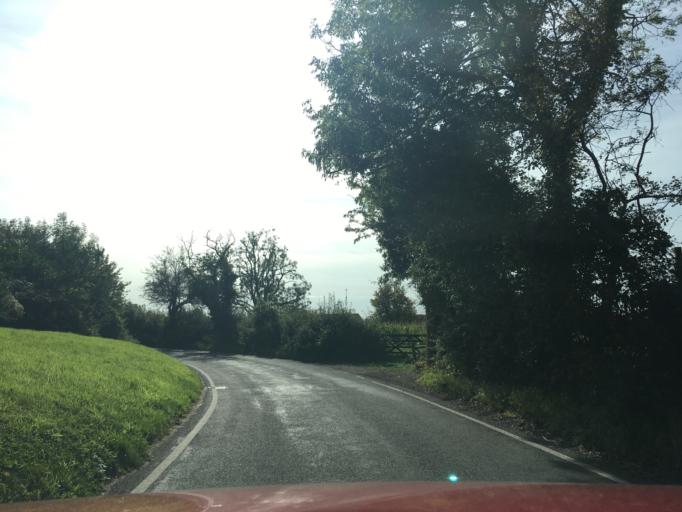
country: GB
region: England
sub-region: South Gloucestershire
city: Chipping Sodbury
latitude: 51.5557
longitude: -2.4036
